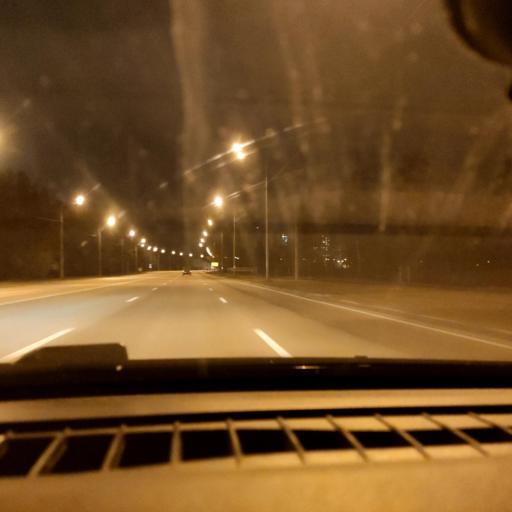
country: RU
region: Voronezj
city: Podgornoye
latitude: 51.7320
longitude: 39.1697
